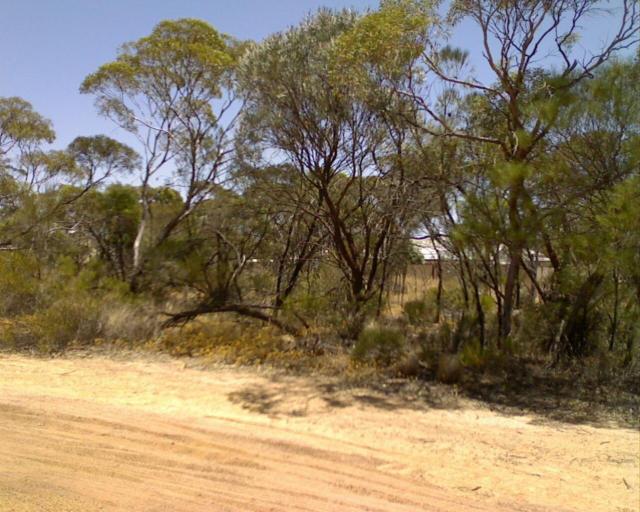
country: AU
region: Western Australia
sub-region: Wongan-Ballidu
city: Wongan Hills
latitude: -30.3668
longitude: 117.1194
